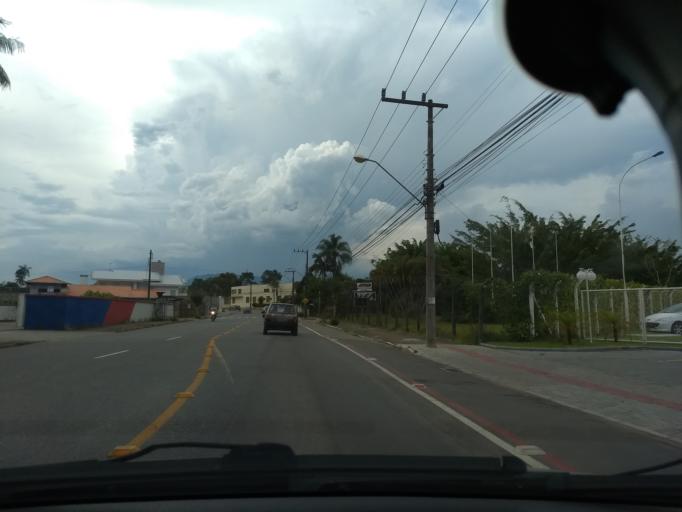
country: BR
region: Santa Catarina
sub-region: Jaragua Do Sul
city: Jaragua do Sul
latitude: -26.4737
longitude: -49.1019
